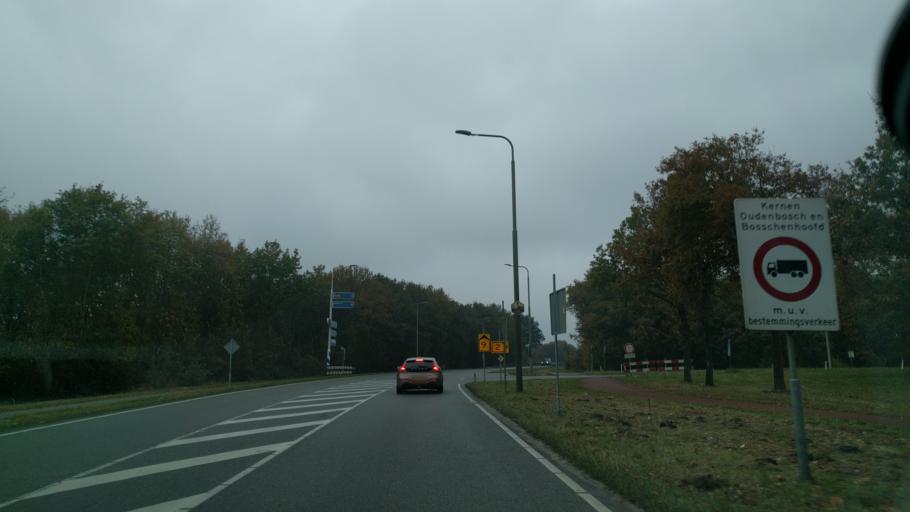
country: NL
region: North Brabant
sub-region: Gemeente Rucphen
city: Rucphen
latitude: 51.5494
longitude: 4.5464
